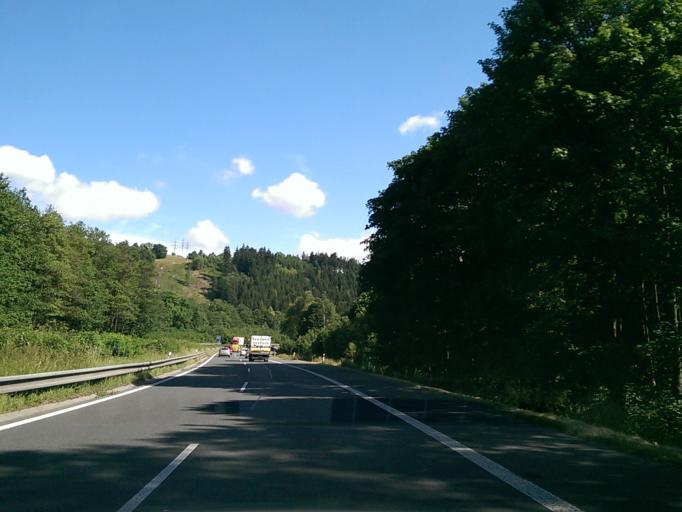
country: CZ
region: Liberecky
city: Hodkovice nad Mohelkou
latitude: 50.6790
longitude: 15.1019
